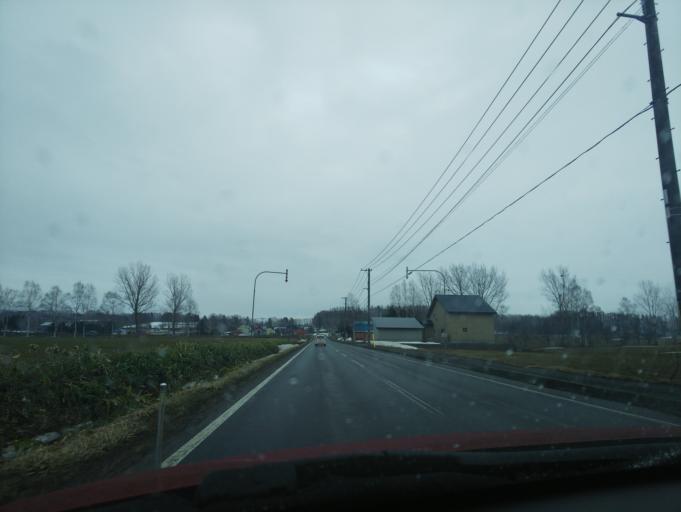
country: JP
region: Hokkaido
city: Nayoro
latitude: 44.3363
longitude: 142.4720
